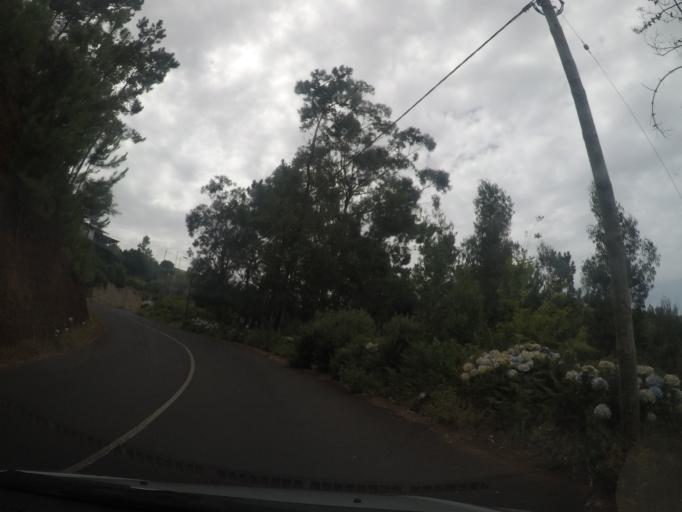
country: PT
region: Madeira
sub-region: Santa Cruz
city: Camacha
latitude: 32.6897
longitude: -16.8319
